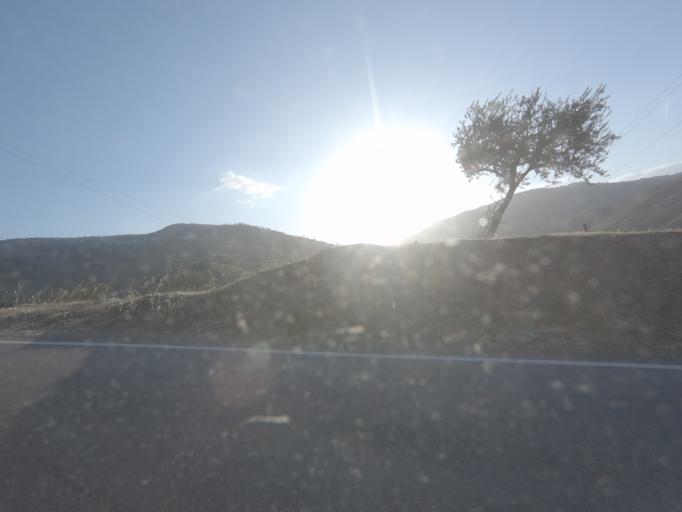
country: PT
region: Viseu
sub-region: Armamar
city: Armamar
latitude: 41.1560
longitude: -7.6383
